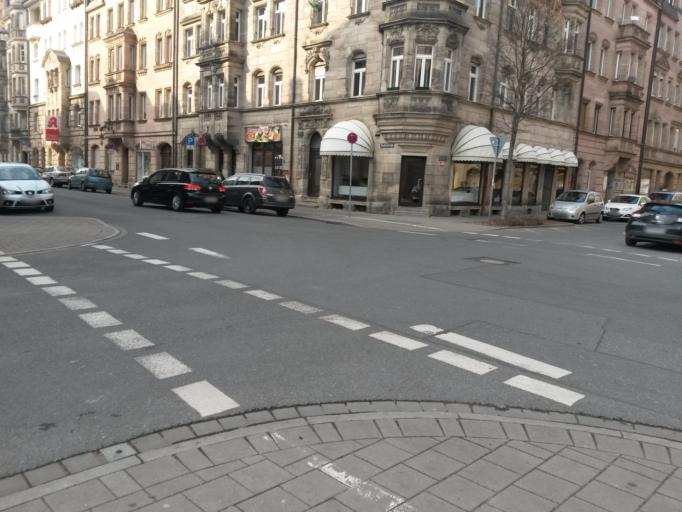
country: DE
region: Bavaria
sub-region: Regierungsbezirk Mittelfranken
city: Furth
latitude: 49.4673
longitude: 10.9916
